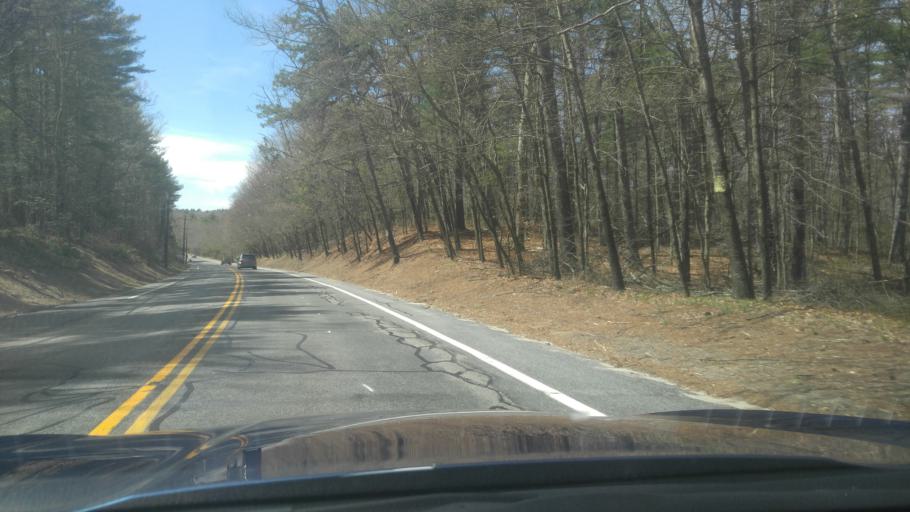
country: US
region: Rhode Island
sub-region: Kent County
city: West Greenwich
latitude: 41.5880
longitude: -71.6214
